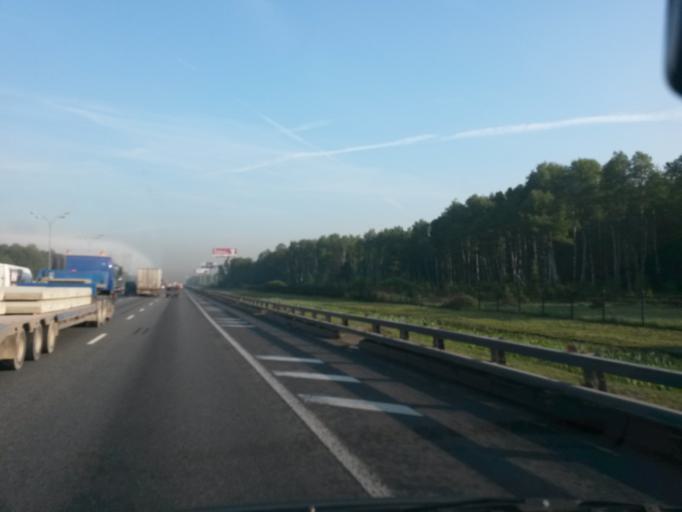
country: RU
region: Moskovskaya
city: Druzhba
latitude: 55.8648
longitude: 37.7608
